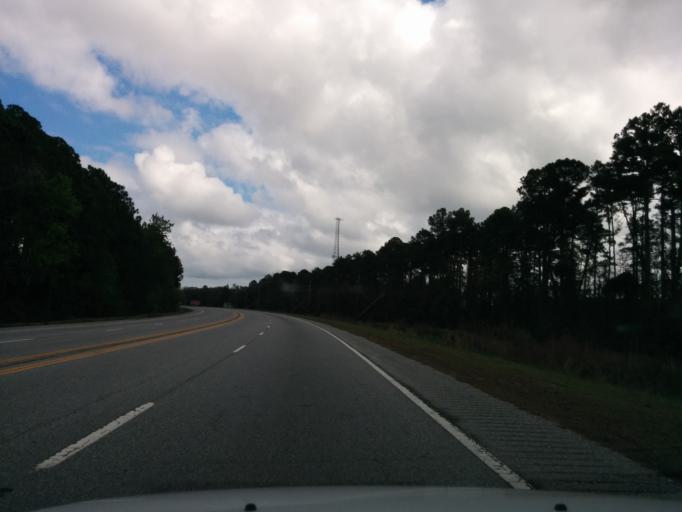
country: US
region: Georgia
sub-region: Glynn County
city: Brunswick
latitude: 31.1153
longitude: -81.5370
